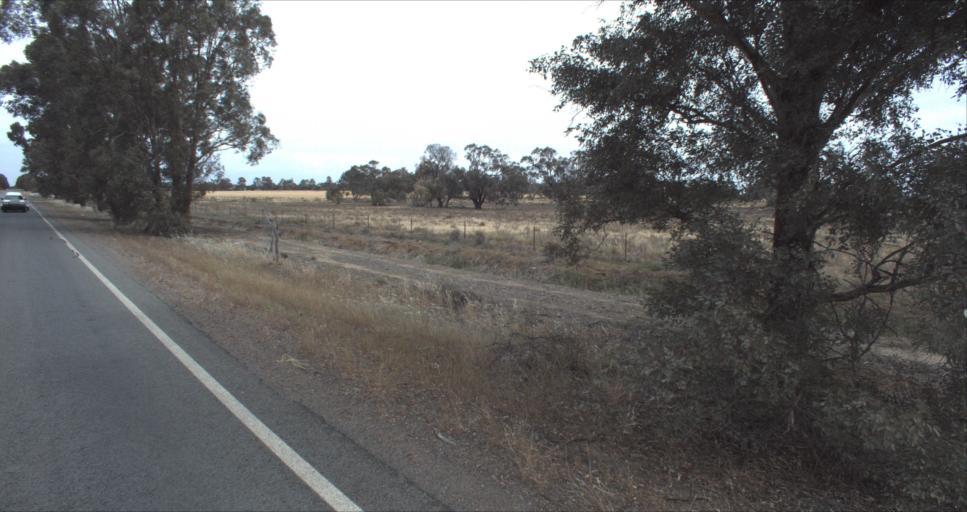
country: AU
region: New South Wales
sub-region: Leeton
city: Leeton
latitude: -34.5135
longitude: 146.4187
